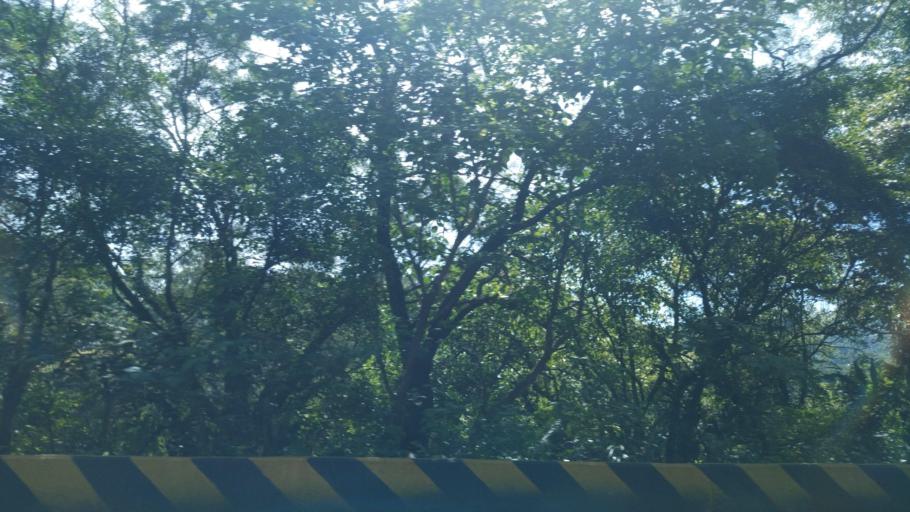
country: TW
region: Taipei
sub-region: Taipei
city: Banqiao
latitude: 24.9470
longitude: 121.5045
